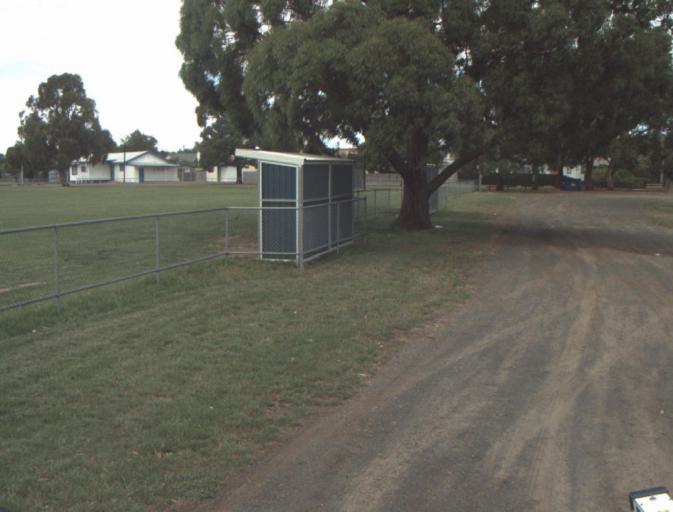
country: AU
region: Tasmania
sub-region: Launceston
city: Newstead
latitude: -41.4357
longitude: 147.1642
